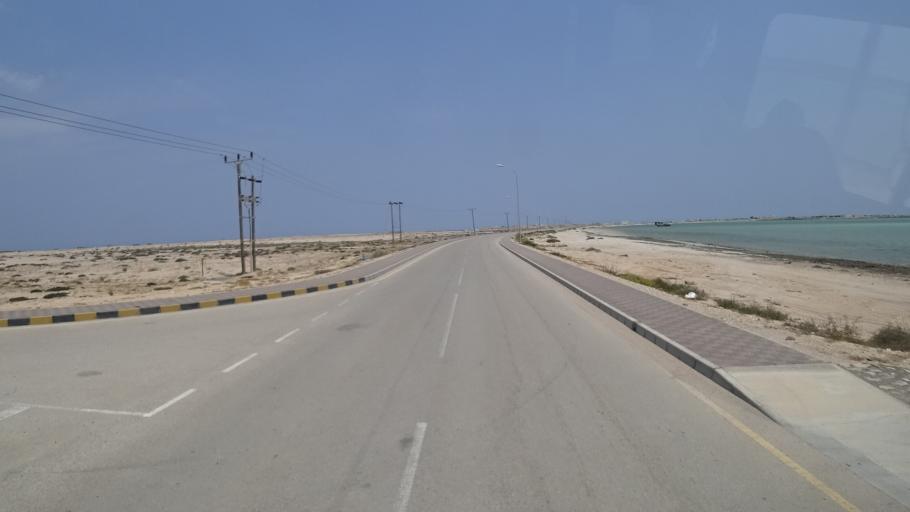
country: OM
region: Ash Sharqiyah
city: Sur
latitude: 22.5282
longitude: 59.7665
